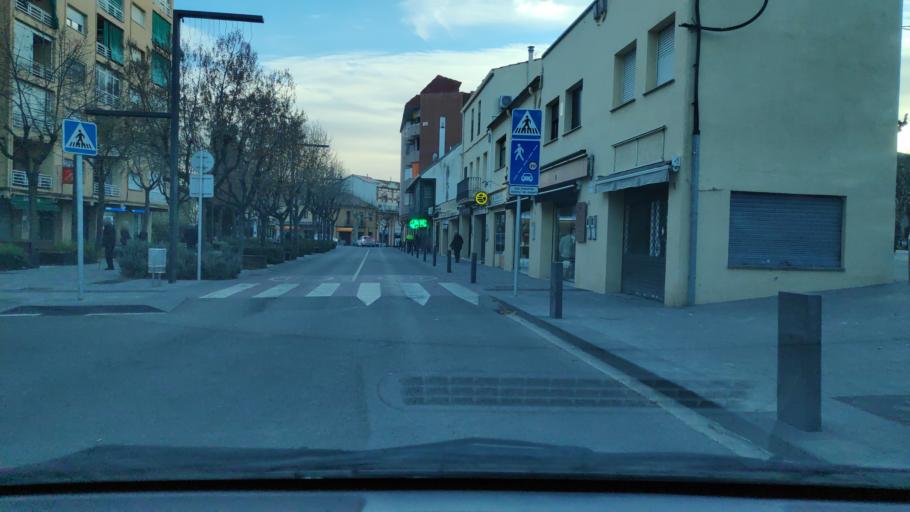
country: ES
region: Catalonia
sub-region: Provincia de Barcelona
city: Montmelo
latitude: 41.5523
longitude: 2.2489
